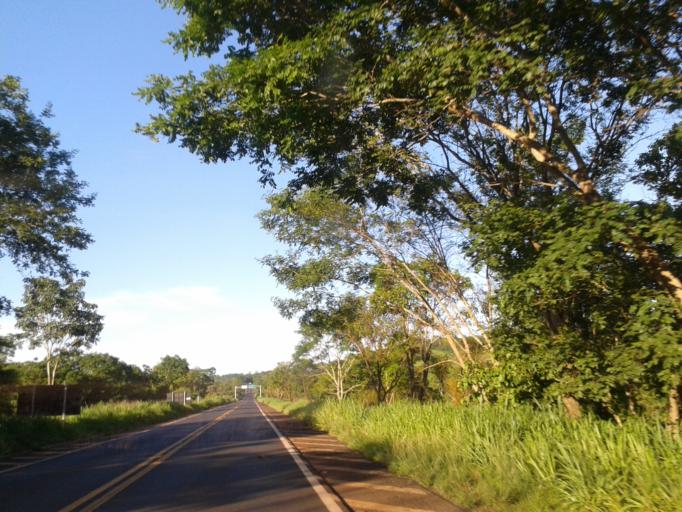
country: BR
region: Minas Gerais
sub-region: Santa Vitoria
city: Santa Vitoria
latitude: -18.9356
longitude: -49.8001
